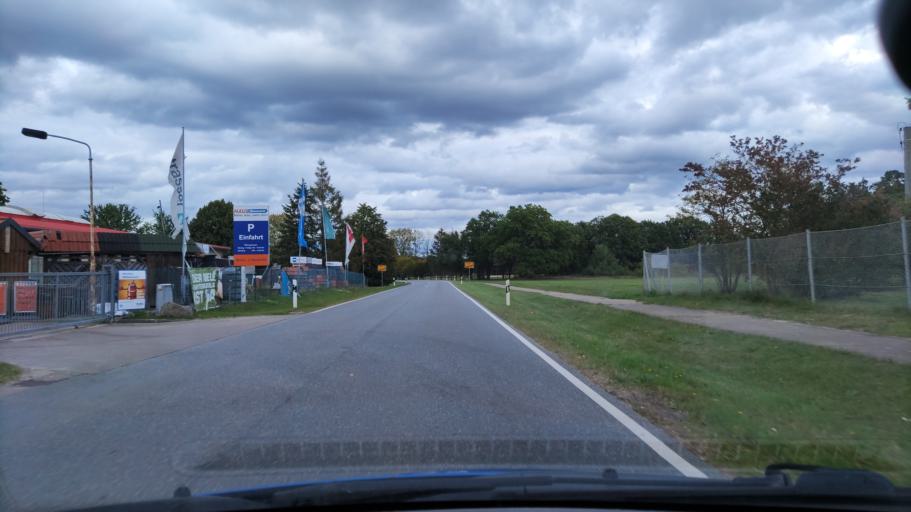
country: DE
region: Lower Saxony
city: Neu Darchau
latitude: 53.2900
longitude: 10.9477
